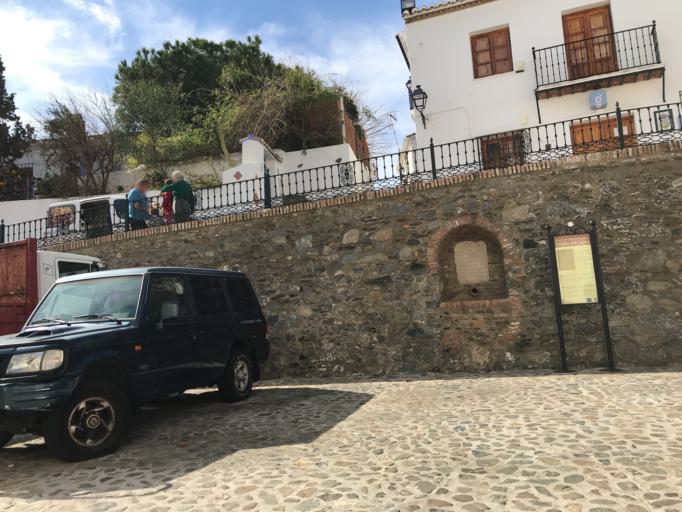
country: ES
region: Andalusia
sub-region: Provincia de Malaga
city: Valdes
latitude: 36.7624
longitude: -4.2138
